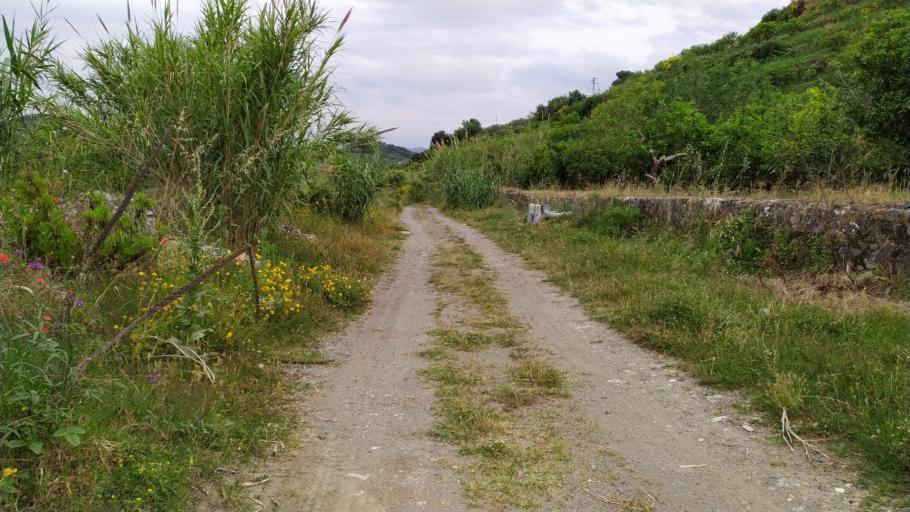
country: IT
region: Sicily
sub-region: Messina
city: San Filippo del Mela
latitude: 38.1724
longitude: 15.2785
